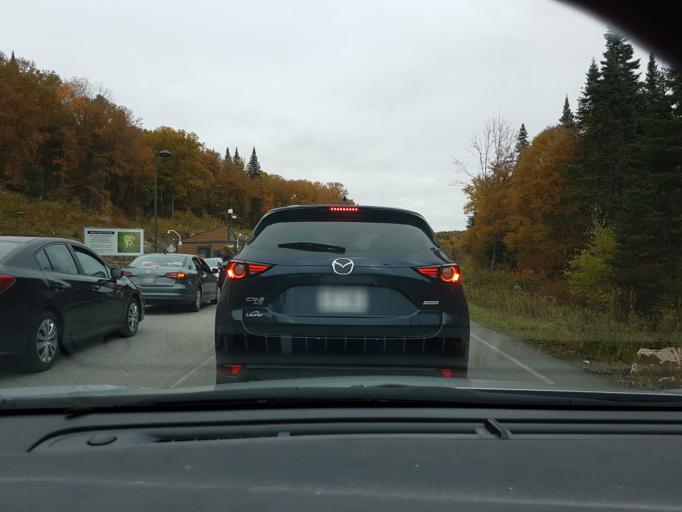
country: CA
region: Quebec
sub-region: Capitale-Nationale
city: Shannon
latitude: 47.1078
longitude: -71.3465
